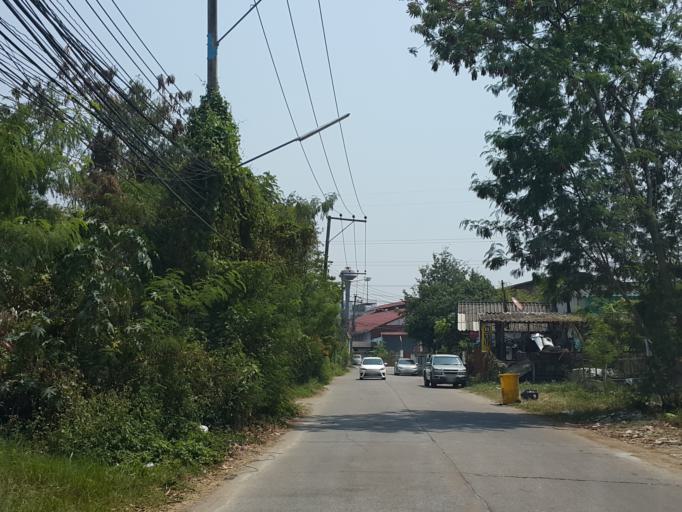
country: TH
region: Chiang Mai
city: Chiang Mai
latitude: 18.7749
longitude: 99.0251
